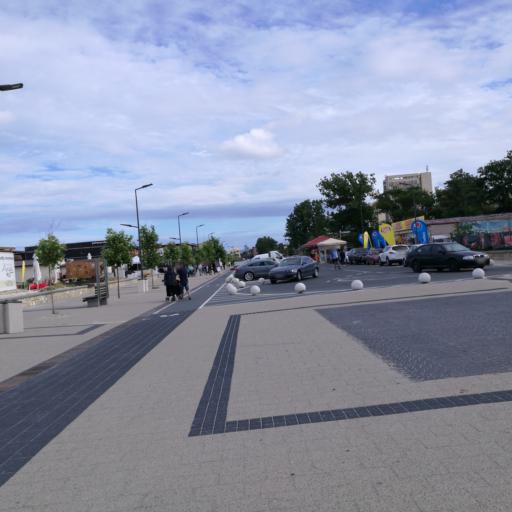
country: RO
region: Constanta
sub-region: Municipiul Constanta
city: Palazu Mare
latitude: 44.2431
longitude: 28.6232
